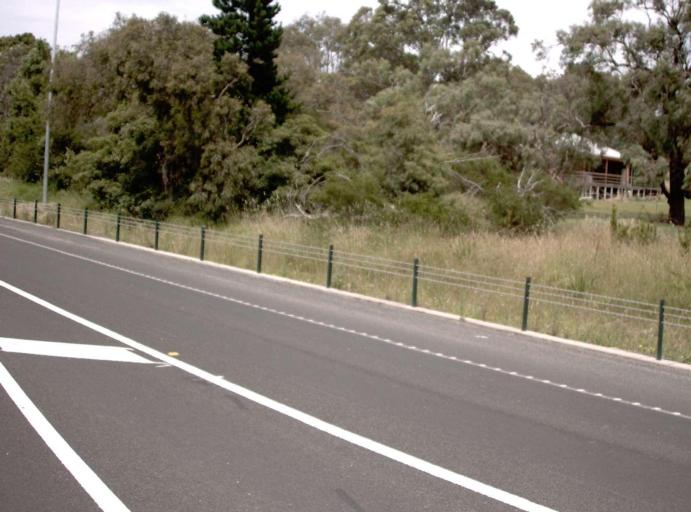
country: AU
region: Victoria
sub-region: Mornington Peninsula
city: Langwarrin South
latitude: -38.1836
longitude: 145.2190
